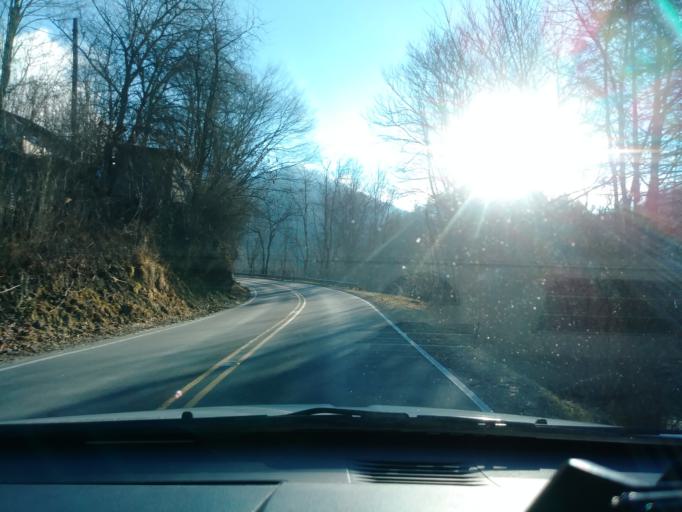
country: US
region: North Carolina
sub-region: Avery County
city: Banner Elk
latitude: 36.1720
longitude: -81.9397
